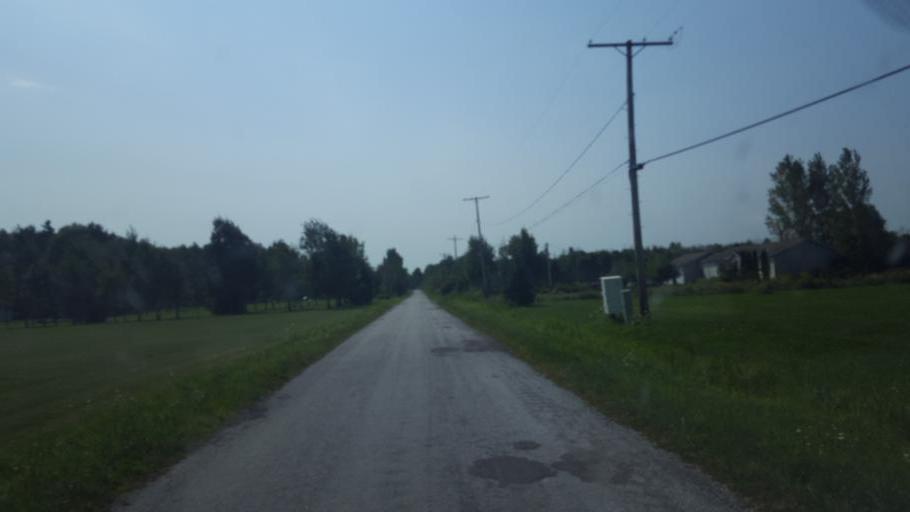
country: US
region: Ohio
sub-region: Ashtabula County
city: Orwell
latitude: 41.5913
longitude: -80.9923
